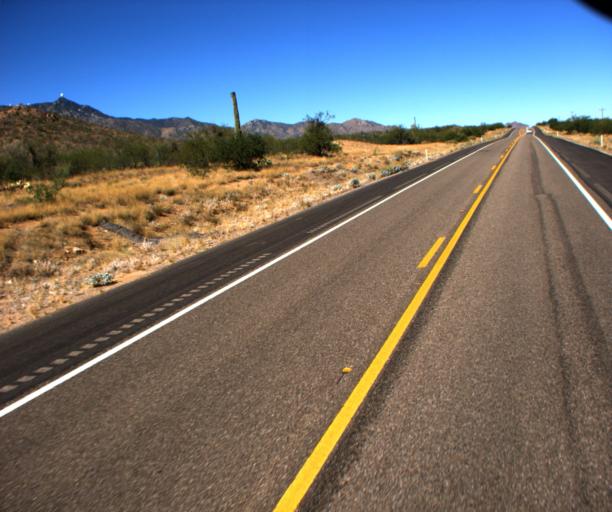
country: US
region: Arizona
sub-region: Pima County
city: Three Points
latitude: 32.0330
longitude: -111.5525
